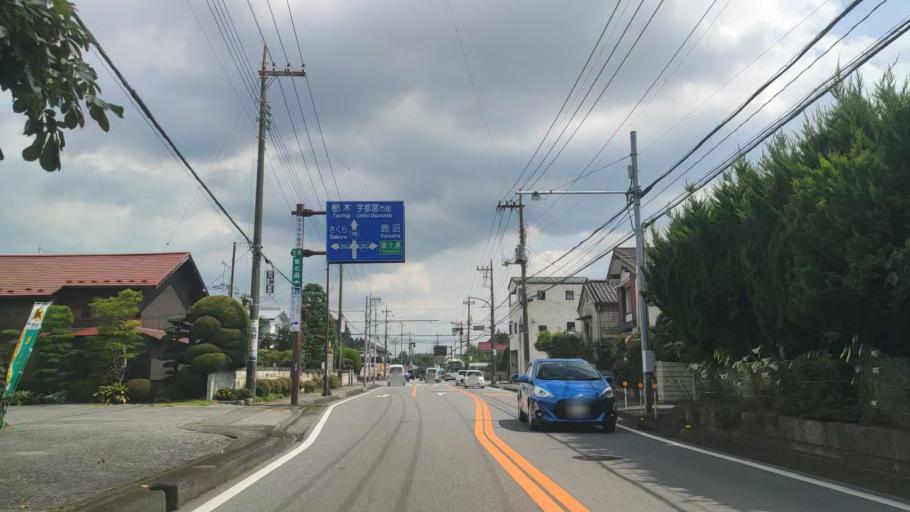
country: JP
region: Tochigi
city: Utsunomiya-shi
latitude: 36.6511
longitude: 139.8436
